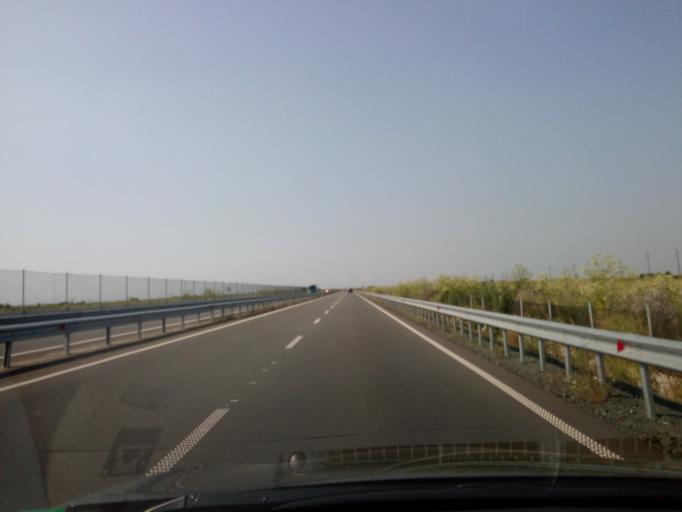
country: BG
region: Burgas
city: Aheloy
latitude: 42.6096
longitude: 27.6217
